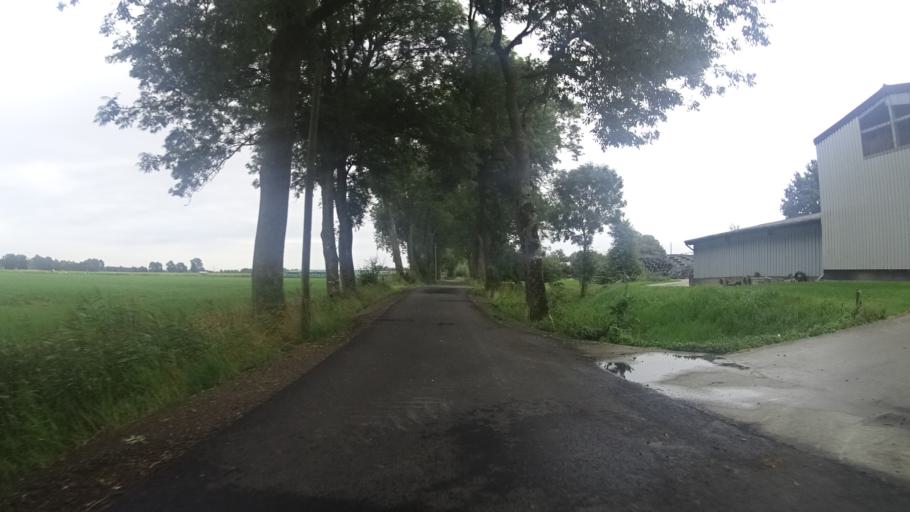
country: DE
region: Schleswig-Holstein
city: Sommerland
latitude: 53.7827
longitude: 9.5475
